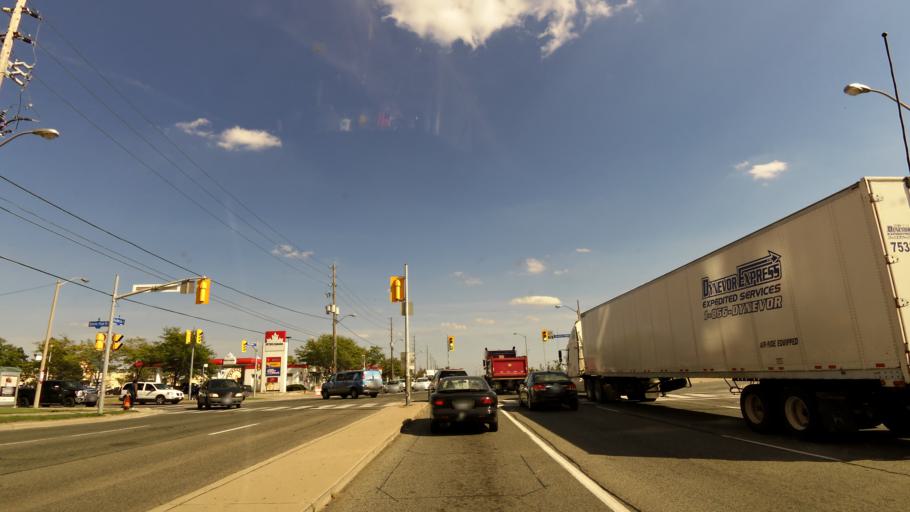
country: CA
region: Ontario
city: Etobicoke
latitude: 43.7193
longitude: -79.6039
